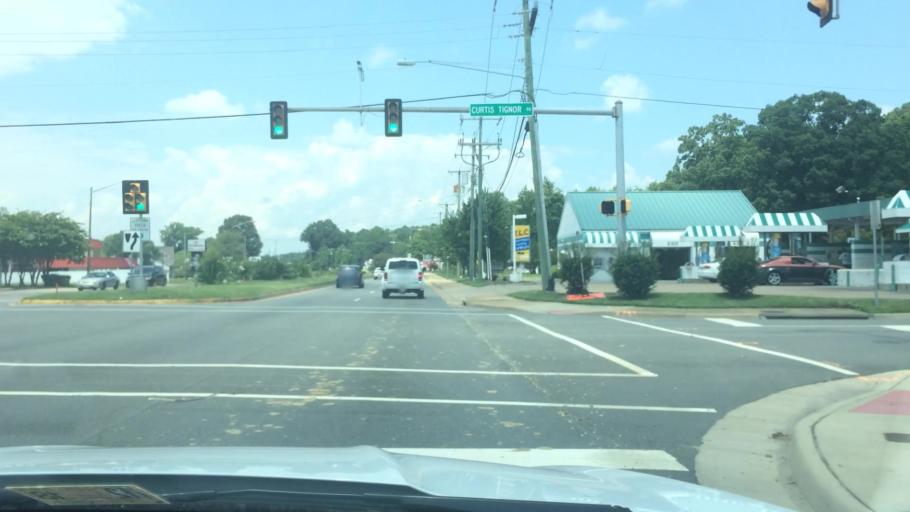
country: US
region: Virginia
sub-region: York County
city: Yorktown
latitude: 37.1433
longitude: -76.5482
